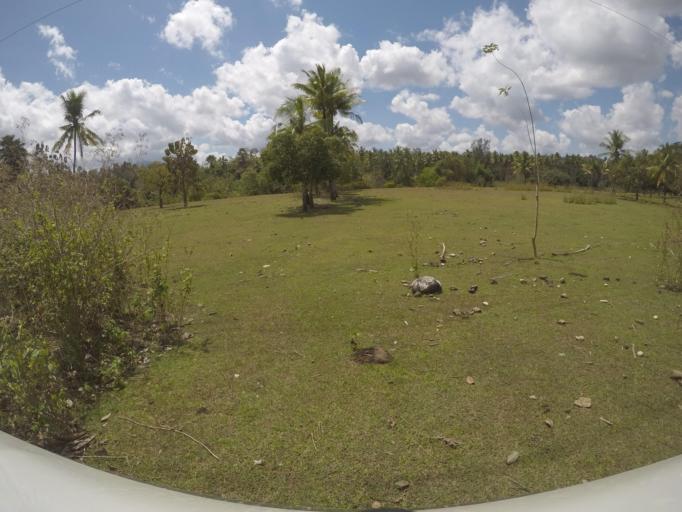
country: TL
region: Viqueque
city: Viqueque
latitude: -8.8390
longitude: 126.3734
